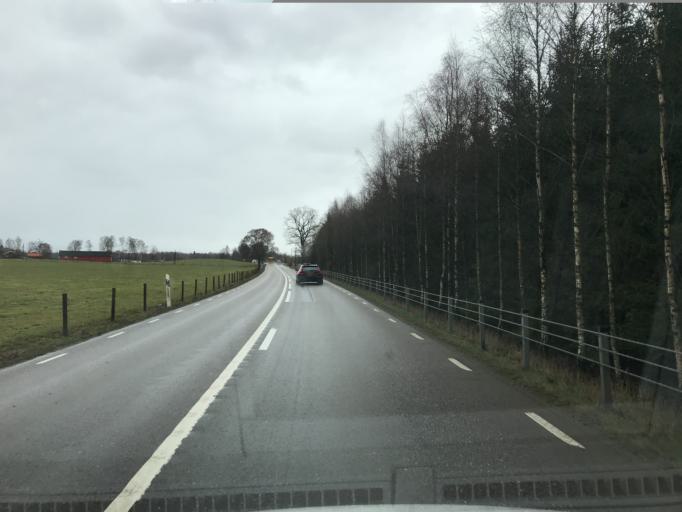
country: SE
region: Skane
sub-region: Klippans Kommun
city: Ljungbyhed
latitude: 56.0992
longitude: 13.1805
